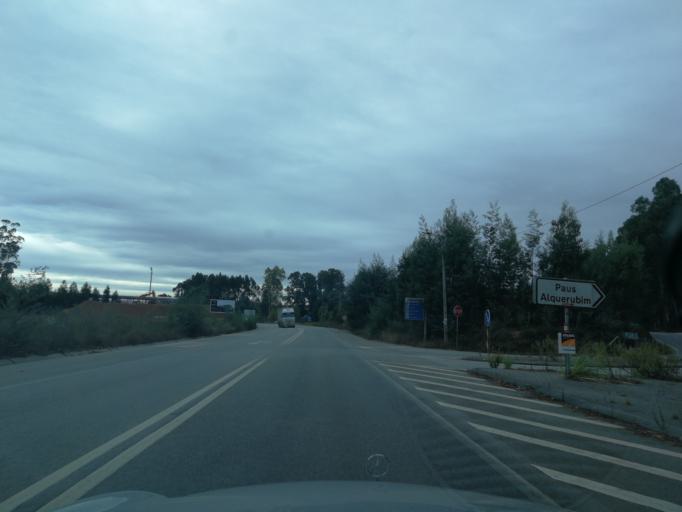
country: PT
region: Aveiro
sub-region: Albergaria-A-Velha
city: Albergaria-a-Velha
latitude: 40.6630
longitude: -8.4754
